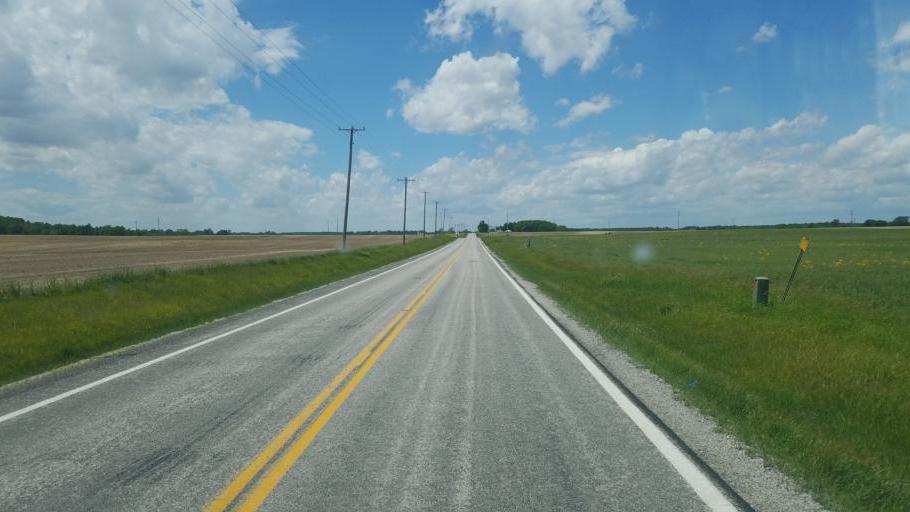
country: US
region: Ohio
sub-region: Huron County
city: Willard
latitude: 41.1051
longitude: -82.6962
